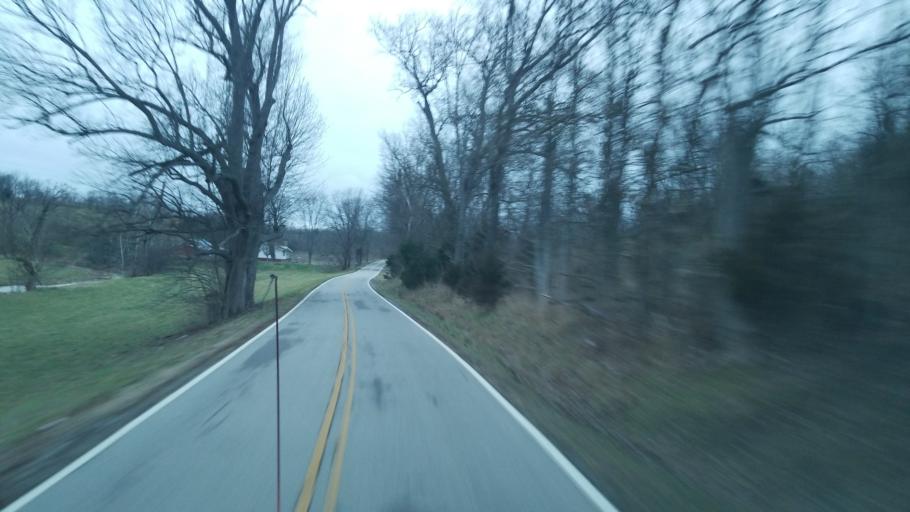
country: US
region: Kentucky
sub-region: Fleming County
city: Flemingsburg
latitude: 38.5241
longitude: -83.6968
